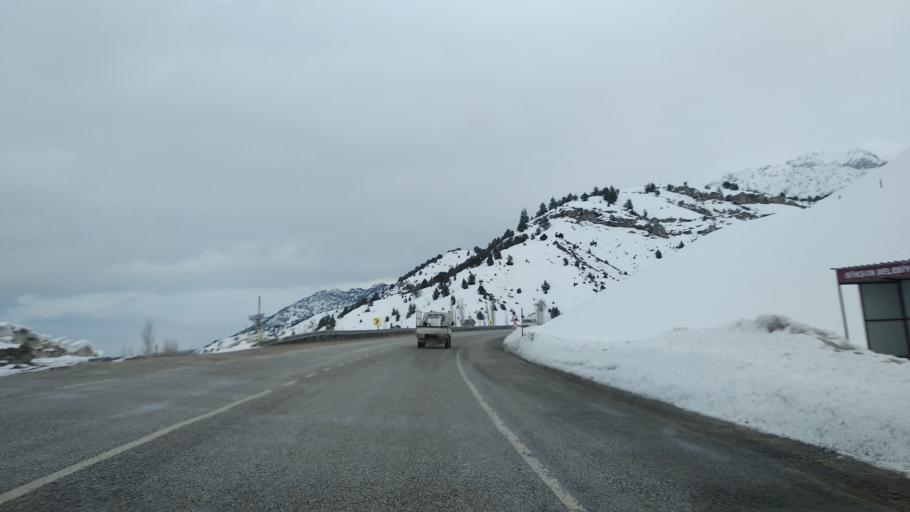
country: TR
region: Kahramanmaras
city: Goksun
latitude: 37.9987
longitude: 36.5344
